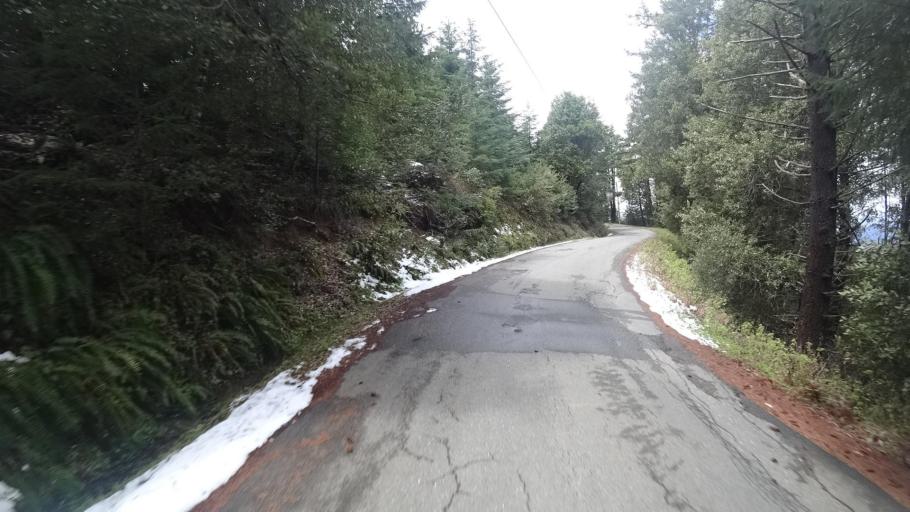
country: US
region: California
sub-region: Humboldt County
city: Blue Lake
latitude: 40.8804
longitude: -123.8809
